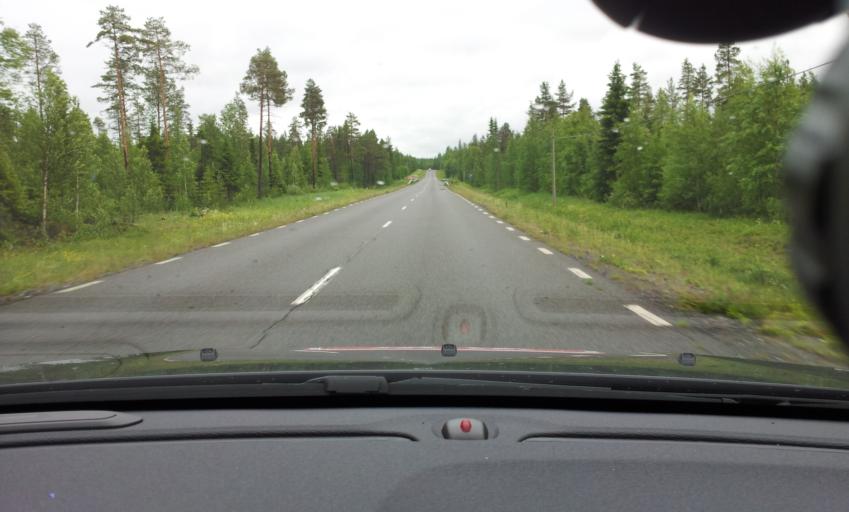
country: SE
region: Jaemtland
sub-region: OEstersunds Kommun
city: Lit
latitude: 63.7045
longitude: 14.9887
